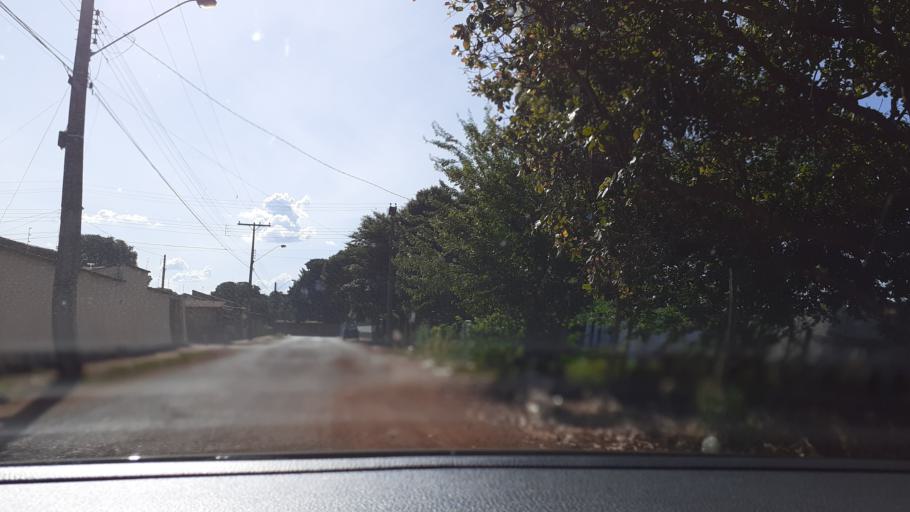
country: BR
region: Goias
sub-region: Itumbiara
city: Itumbiara
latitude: -18.4112
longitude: -49.2541
